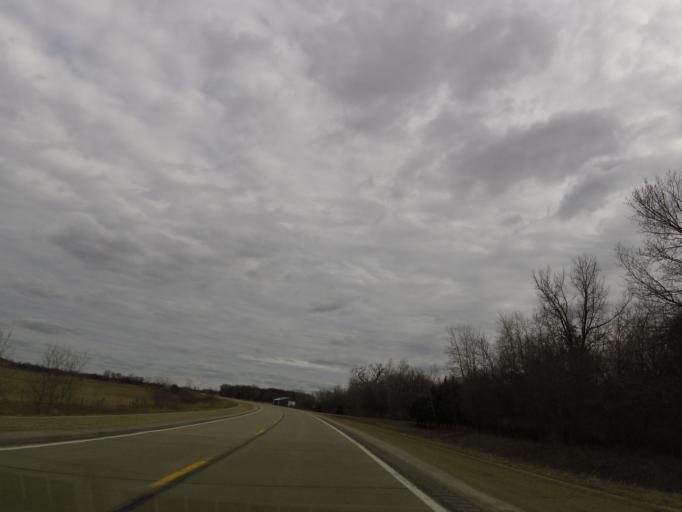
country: US
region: Minnesota
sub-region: Fillmore County
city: Spring Valley
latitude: 43.4835
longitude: -92.3507
